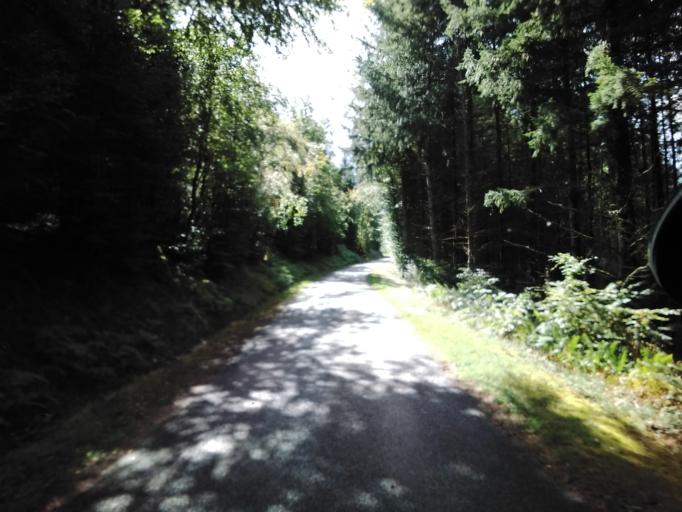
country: FR
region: Bourgogne
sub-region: Departement de la Nievre
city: Lormes
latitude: 47.3240
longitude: 3.8979
